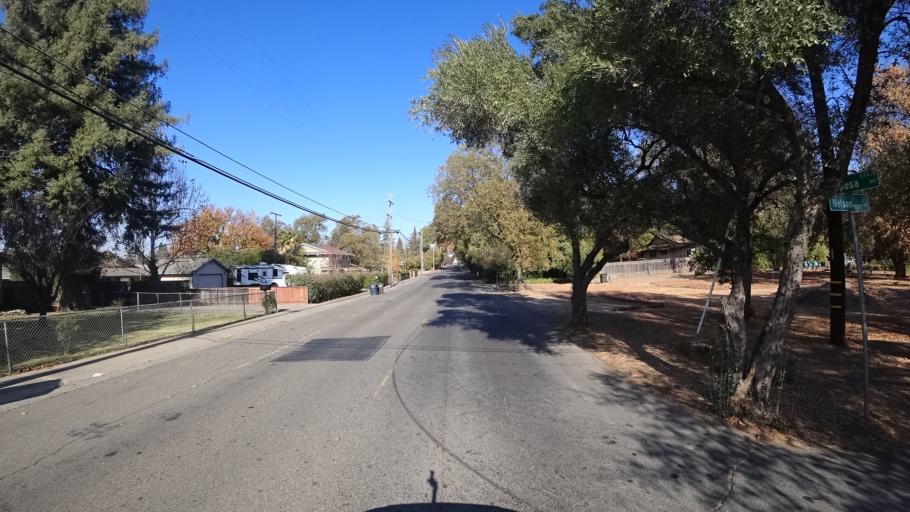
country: US
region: California
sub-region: Sacramento County
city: Citrus Heights
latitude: 38.6937
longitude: -121.2811
